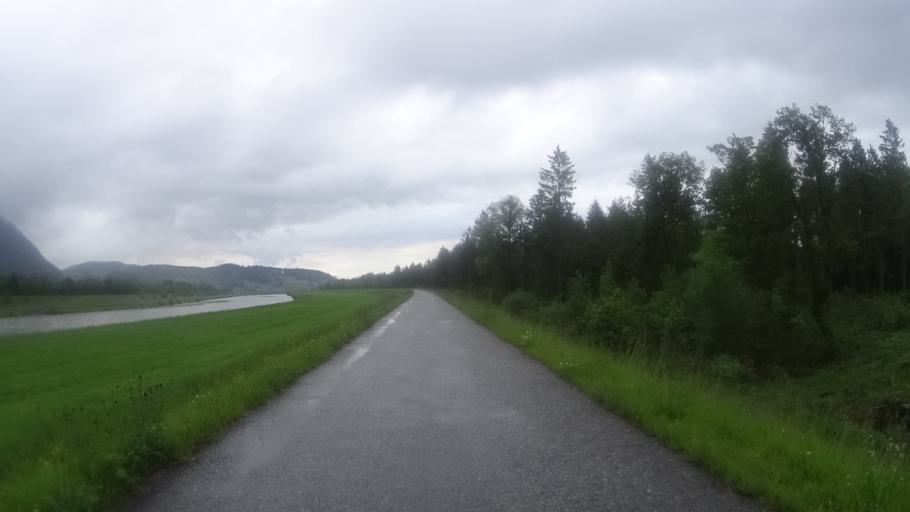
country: CH
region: Saint Gallen
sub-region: Wahlkreis Rheintal
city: Ruthi
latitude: 47.2839
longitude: 9.5512
